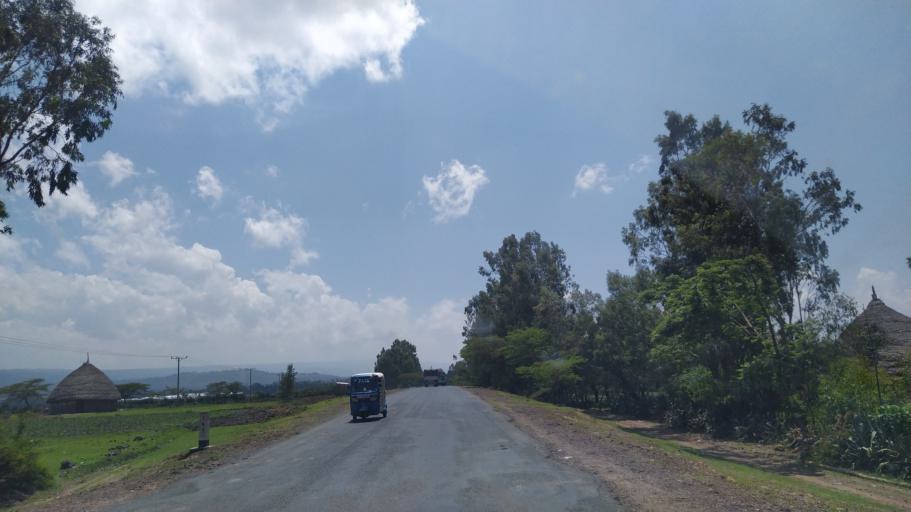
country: ET
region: Southern Nations, Nationalities, and People's Region
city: Butajira
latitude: 7.7635
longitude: 38.1346
